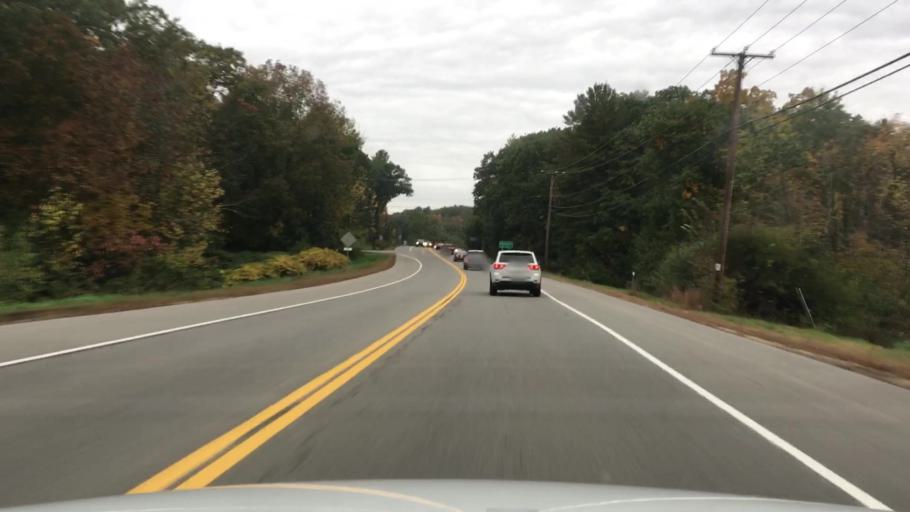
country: US
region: New Hampshire
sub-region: Strafford County
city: Durham
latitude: 43.1378
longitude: -70.9025
